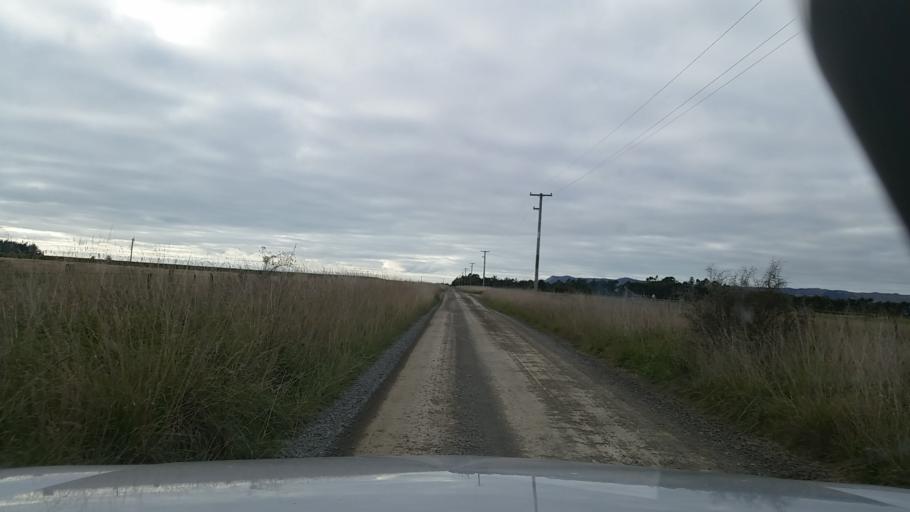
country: NZ
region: Marlborough
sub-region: Marlborough District
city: Blenheim
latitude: -41.5098
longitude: 174.0330
